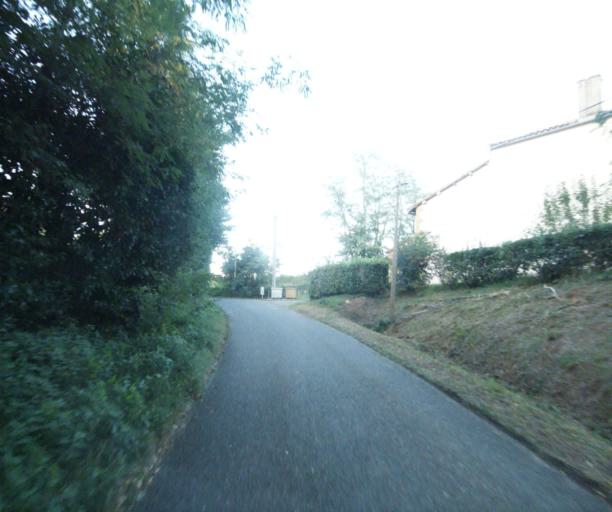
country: FR
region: Midi-Pyrenees
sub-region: Departement du Gers
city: Nogaro
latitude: 43.8309
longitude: -0.0849
